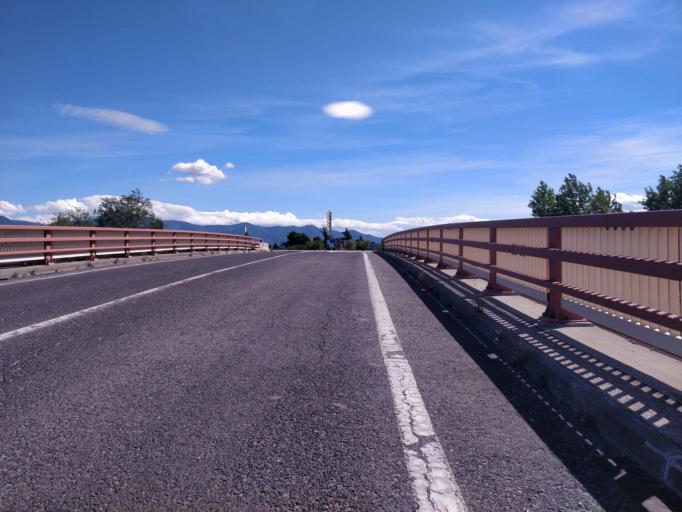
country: FR
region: Languedoc-Roussillon
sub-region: Departement des Pyrenees-Orientales
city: Corneilla-del-Vercol
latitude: 42.6164
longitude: 2.9577
